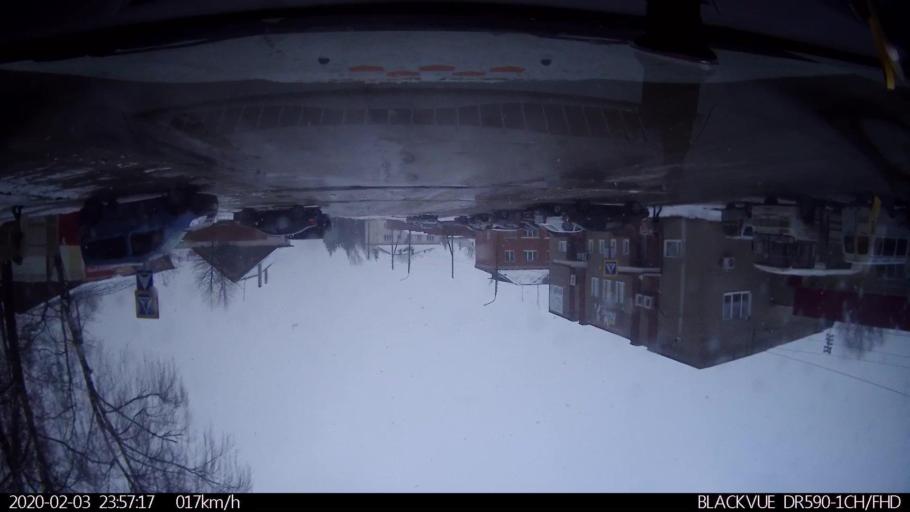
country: RU
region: Nizjnij Novgorod
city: Dal'neye Konstantinovo
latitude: 55.8116
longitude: 44.0946
